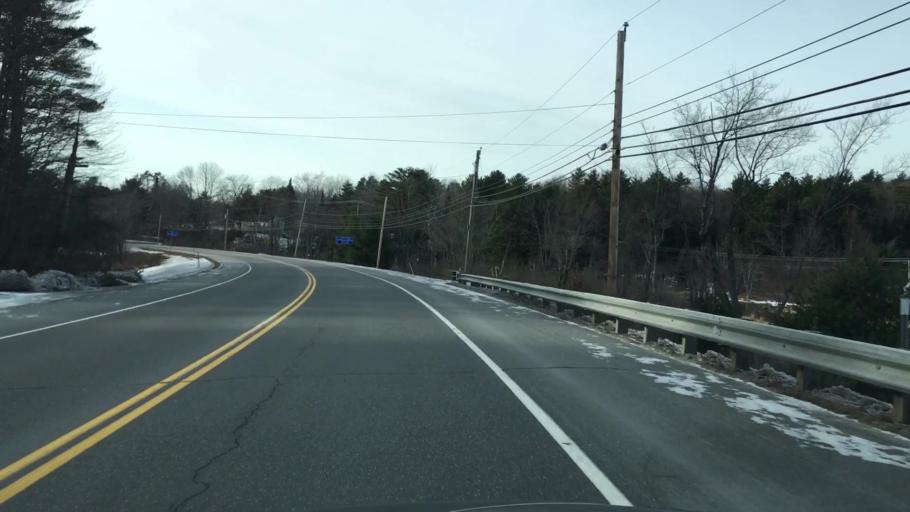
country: US
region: New Hampshire
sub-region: Sullivan County
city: Sunapee
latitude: 43.3790
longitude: -72.1173
